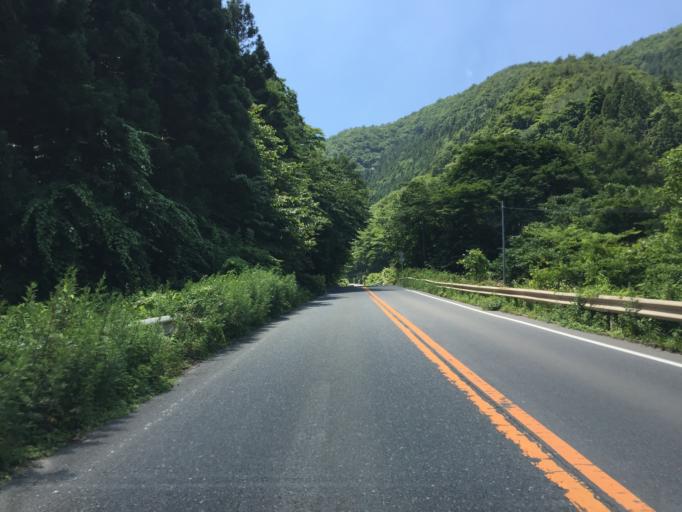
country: JP
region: Miyagi
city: Marumori
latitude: 37.7750
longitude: 140.7998
